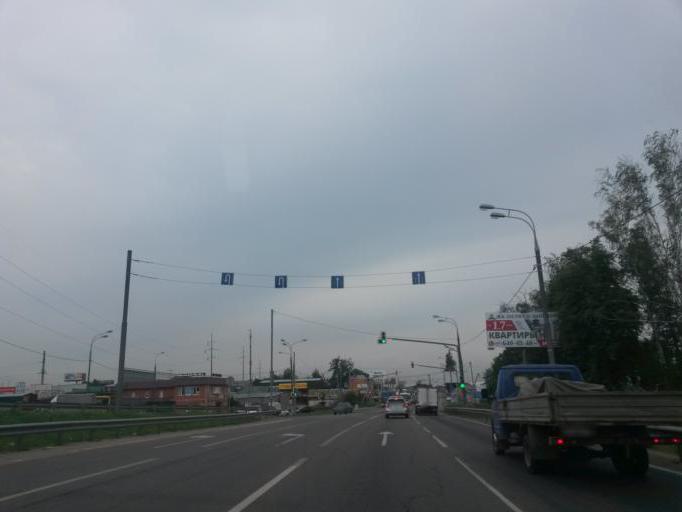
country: RU
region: Moskovskaya
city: Razvilka
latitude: 55.5755
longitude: 37.7567
